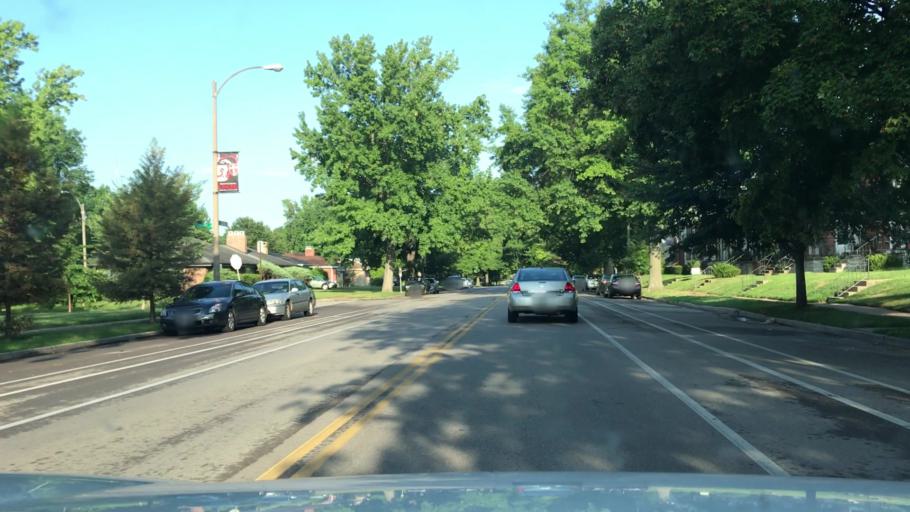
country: US
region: Missouri
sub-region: Saint Louis County
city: Shrewsbury
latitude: 38.5818
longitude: -90.2968
